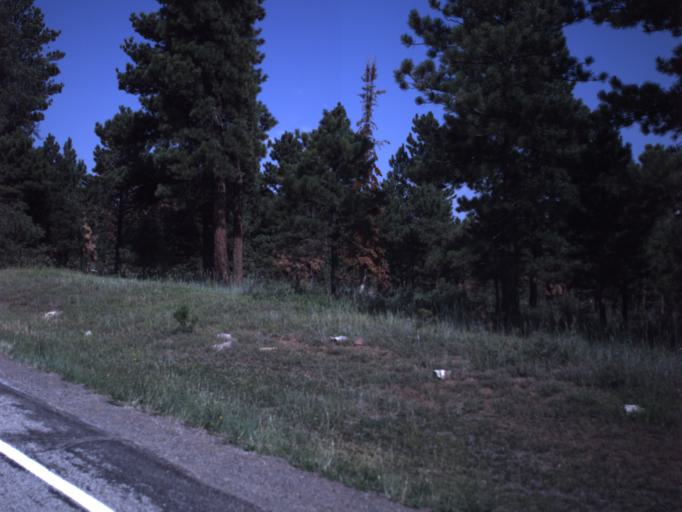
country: US
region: Utah
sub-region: Daggett County
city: Manila
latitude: 40.8609
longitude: -109.5449
